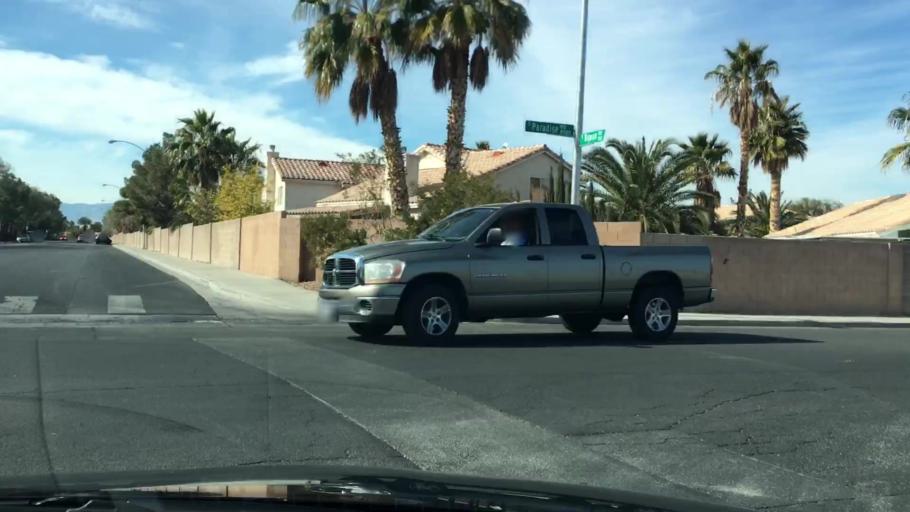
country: US
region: Nevada
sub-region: Clark County
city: Paradise
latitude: 36.0353
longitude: -115.1406
